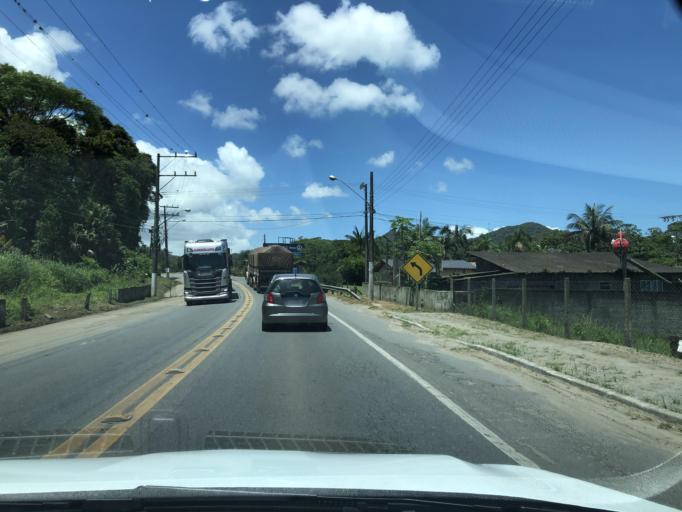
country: BR
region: Santa Catarina
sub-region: Sao Francisco Do Sul
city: Sao Francisco do Sul
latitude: -26.2779
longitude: -48.6462
